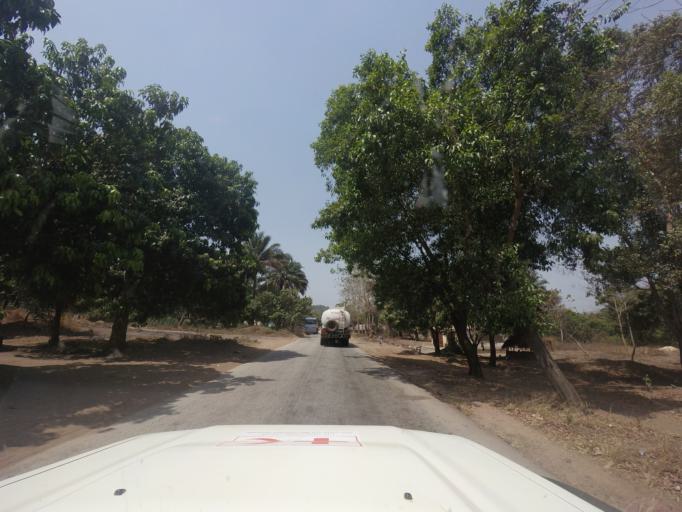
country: GN
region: Kindia
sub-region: Kindia
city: Kindia
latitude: 9.9033
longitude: -13.0180
